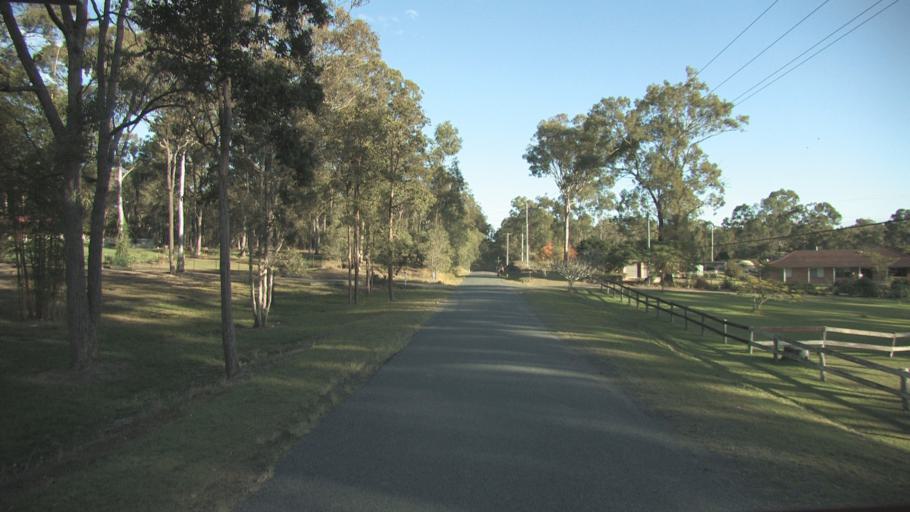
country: AU
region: Queensland
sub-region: Logan
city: Waterford West
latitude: -27.7337
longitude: 153.1515
